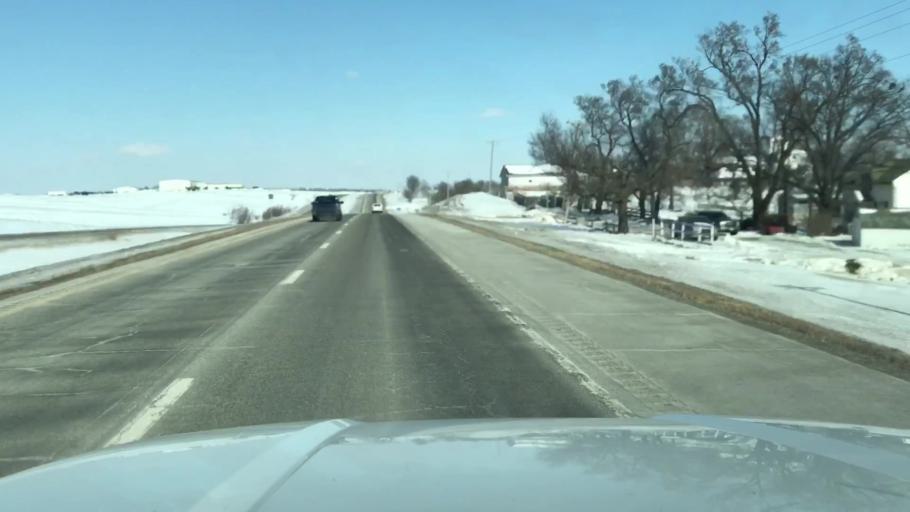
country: US
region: Missouri
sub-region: Nodaway County
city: Maryville
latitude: 40.2920
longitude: -94.8751
